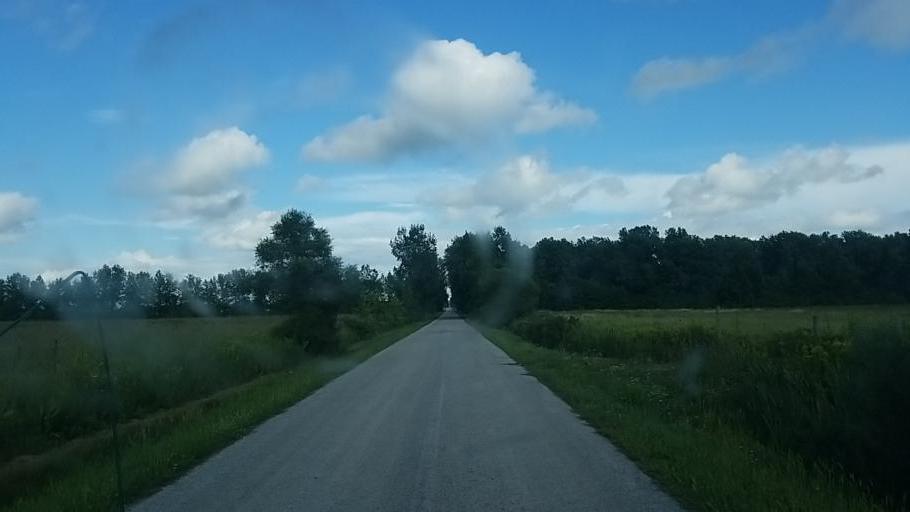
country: US
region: Ohio
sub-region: Hardin County
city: Forest
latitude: 40.7597
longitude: -83.4946
